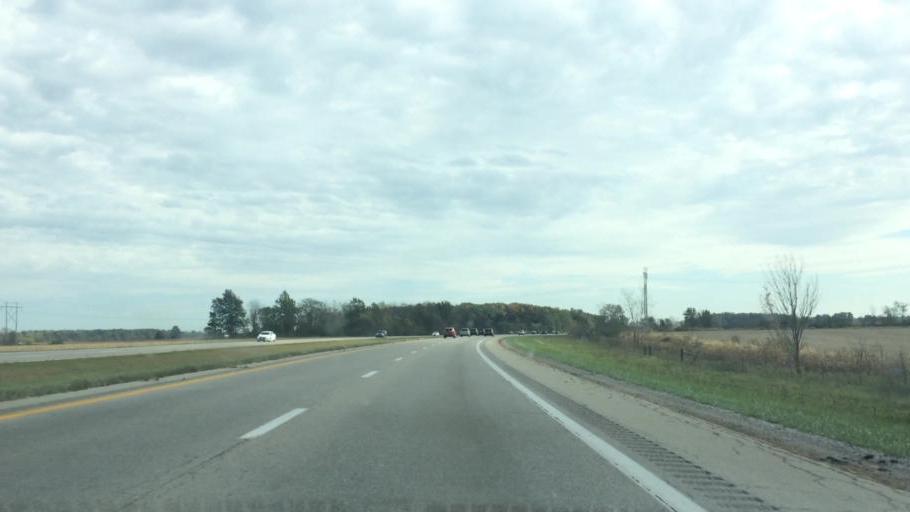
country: US
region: Ohio
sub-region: Union County
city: New California
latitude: 40.1837
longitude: -83.2534
